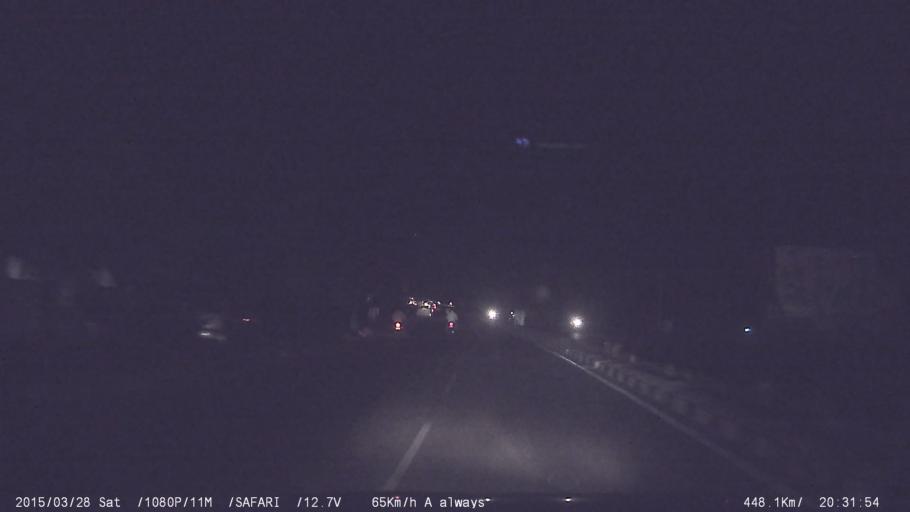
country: IN
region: Karnataka
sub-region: Mandya
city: Maddur
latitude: 12.6177
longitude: 77.0891
